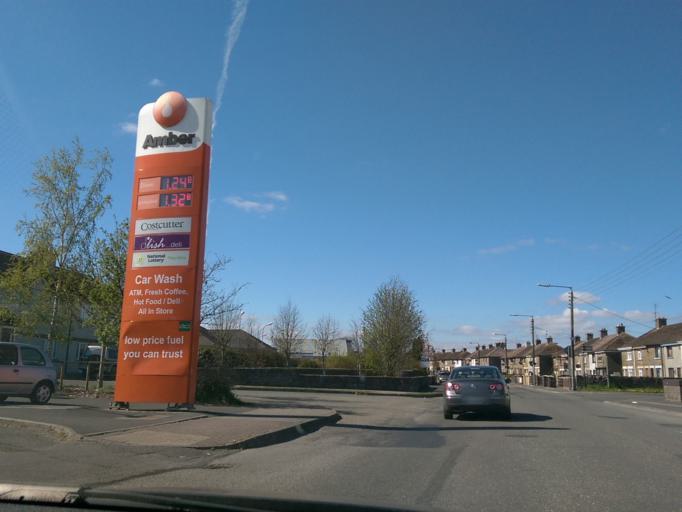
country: IE
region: Leinster
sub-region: Kildare
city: Athy
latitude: 52.9953
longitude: -6.9913
